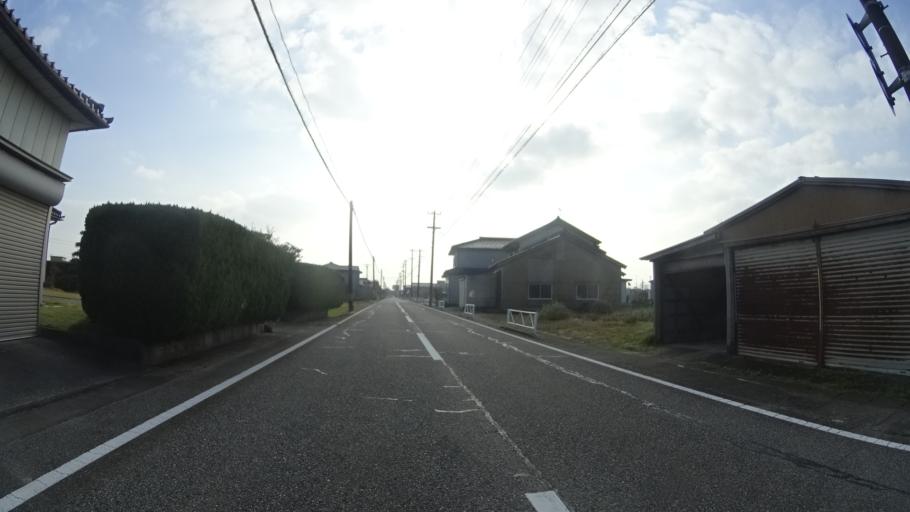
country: JP
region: Toyama
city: Himi
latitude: 36.8745
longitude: 136.9781
